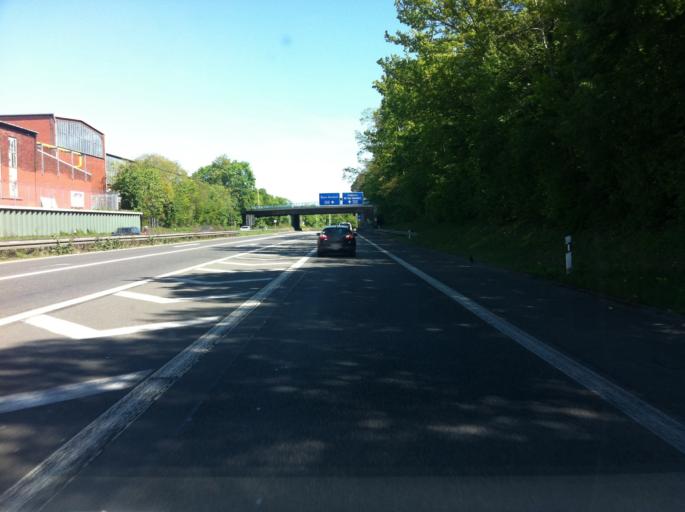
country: DE
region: North Rhine-Westphalia
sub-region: Regierungsbezirk Koln
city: Bonn
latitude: 50.7482
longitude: 7.0668
